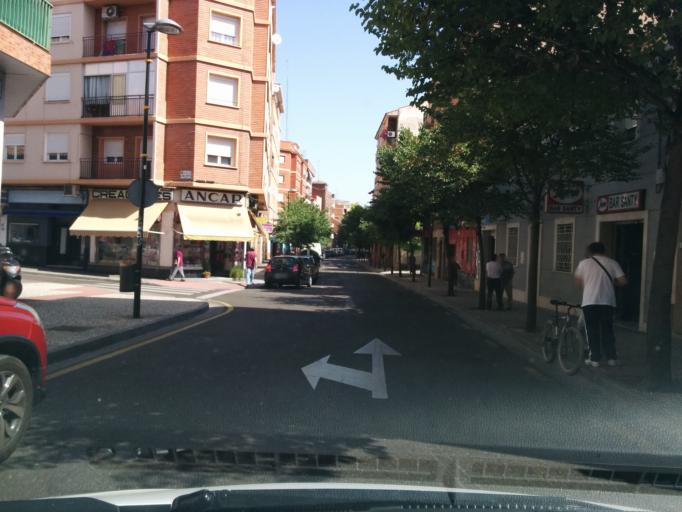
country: ES
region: Aragon
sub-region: Provincia de Zaragoza
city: Zaragoza
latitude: 41.6286
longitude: -0.8840
